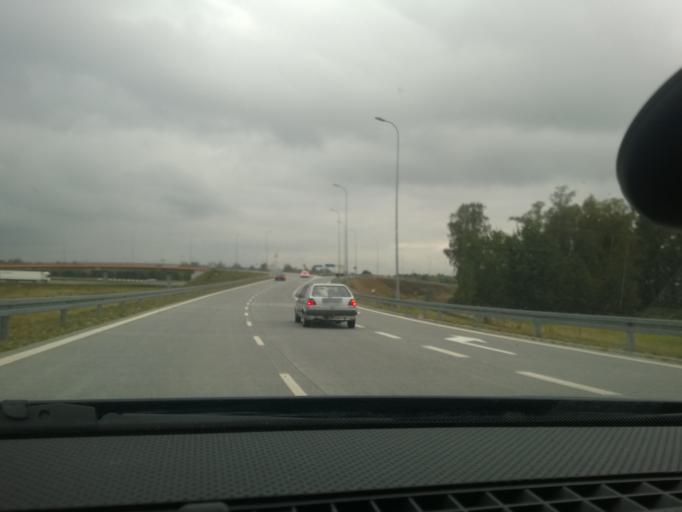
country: PL
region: Lodz Voivodeship
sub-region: Powiat lodzki wschodni
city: Tuszyn
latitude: 51.6381
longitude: 19.5690
